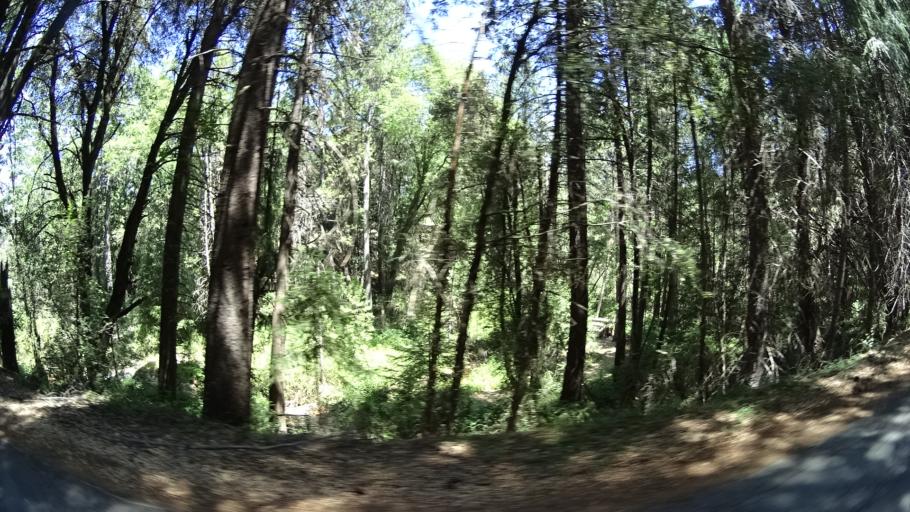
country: US
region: California
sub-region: Amador County
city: Pioneer
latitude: 38.4139
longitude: -120.5235
